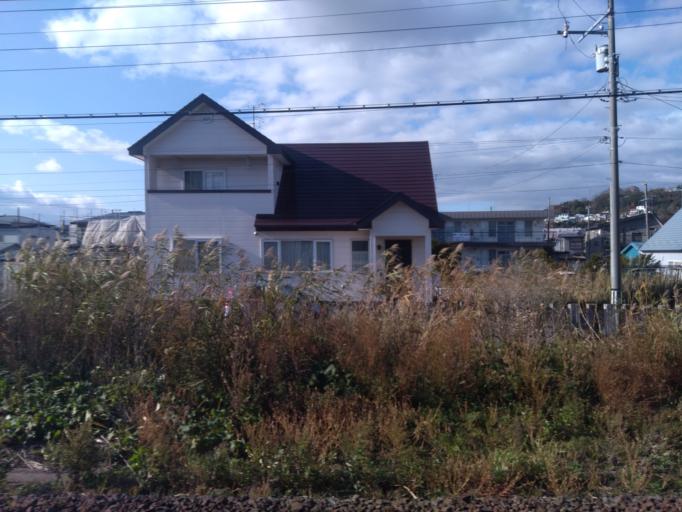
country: JP
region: Hokkaido
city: Muroran
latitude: 42.3530
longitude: 141.0312
